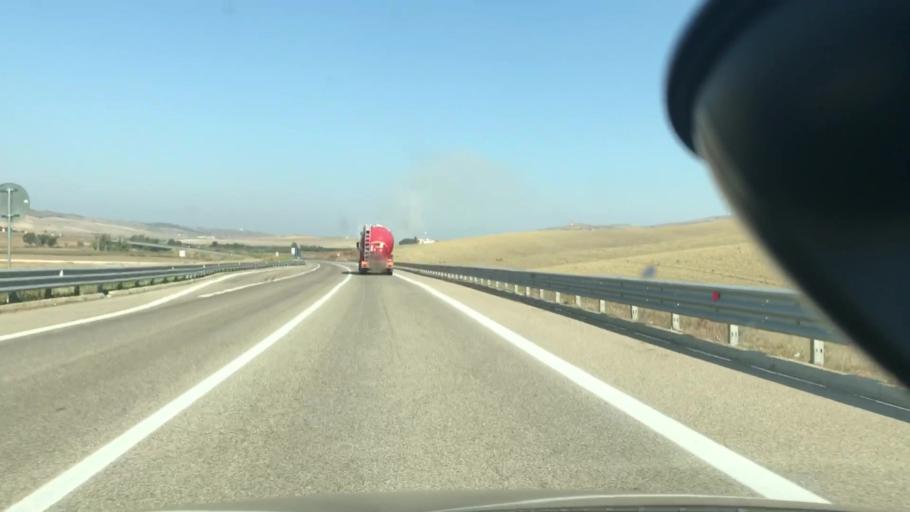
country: IT
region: Basilicate
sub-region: Provincia di Matera
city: Irsina
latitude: 40.7780
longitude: 16.3179
